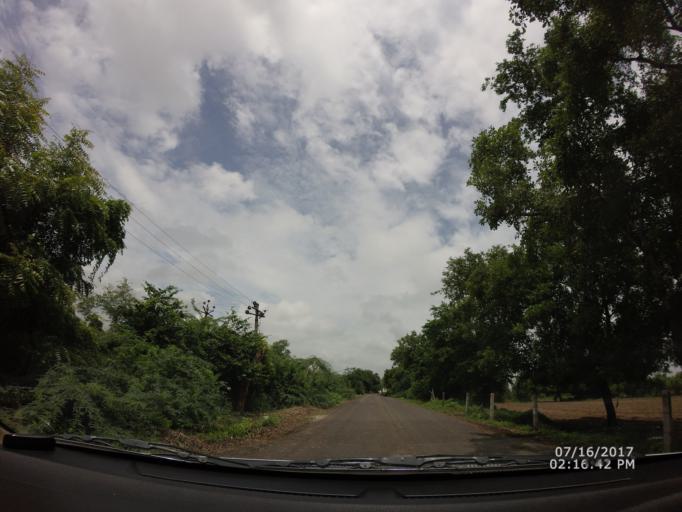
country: IN
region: Gujarat
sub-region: Mahesana
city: Kadi
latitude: 23.1419
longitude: 72.2609
